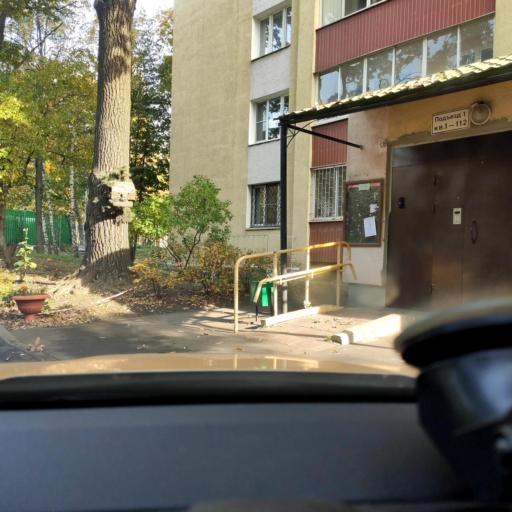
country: RU
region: Moscow
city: Ryazanskiy
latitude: 55.7300
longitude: 37.7671
